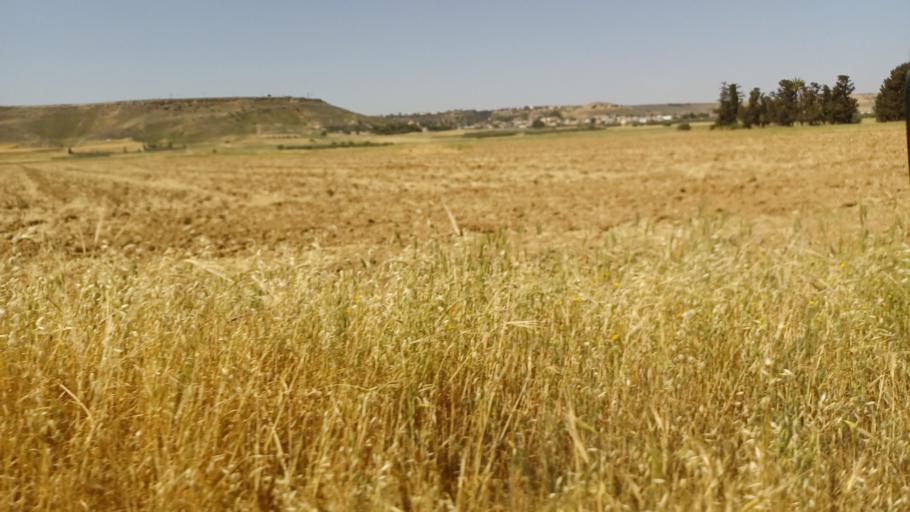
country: CY
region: Lefkosia
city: Mammari
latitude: 35.1832
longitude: 33.2196
